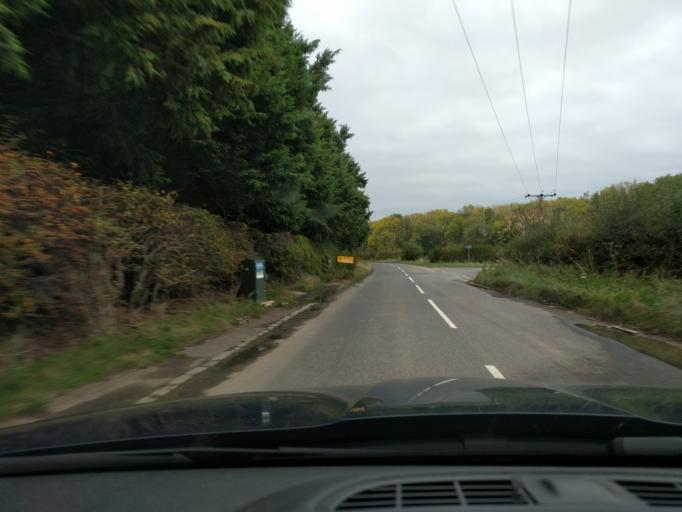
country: GB
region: Scotland
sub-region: The Scottish Borders
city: Allanton
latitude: 55.7160
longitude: -2.1489
